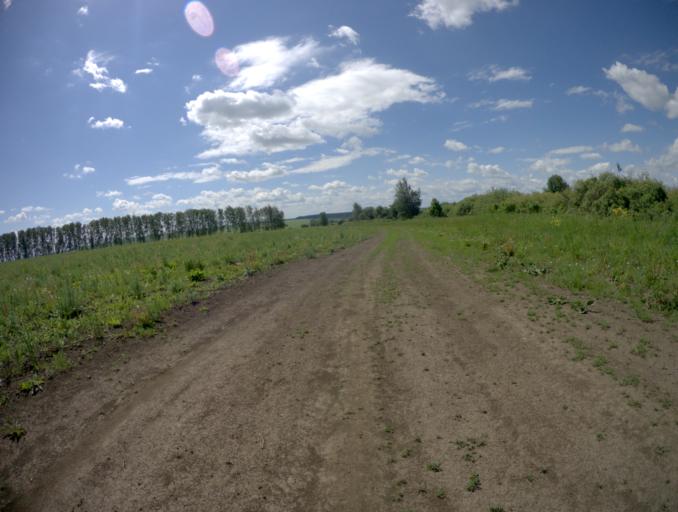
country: RU
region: Ivanovo
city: Gavrilov Posad
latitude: 56.4548
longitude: 40.2218
